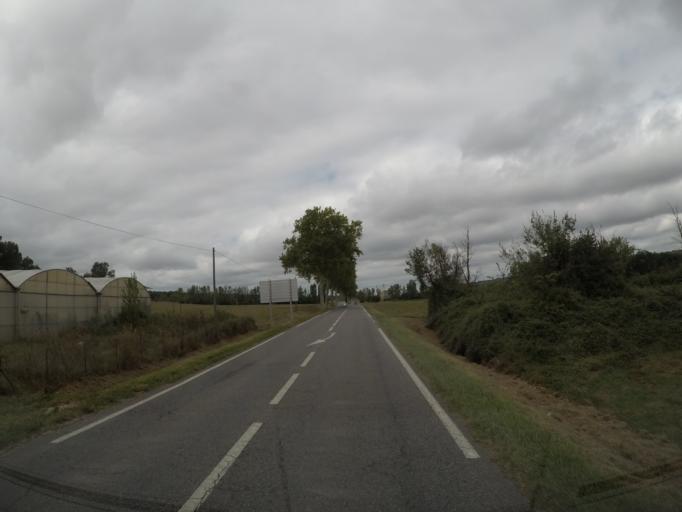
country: FR
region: Midi-Pyrenees
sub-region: Departement de l'Ariege
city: Lezat-sur-Leze
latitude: 43.2332
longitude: 1.3745
